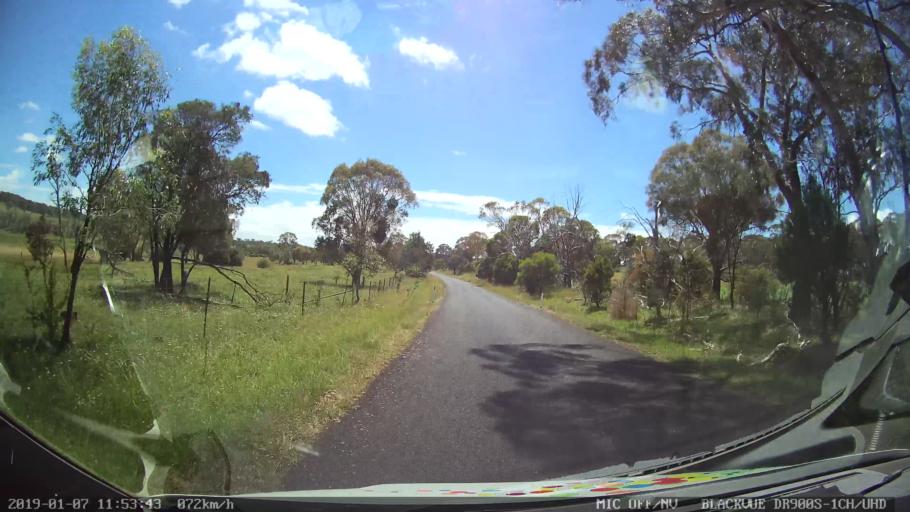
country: AU
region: New South Wales
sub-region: Guyra
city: Guyra
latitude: -30.3026
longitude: 151.6603
